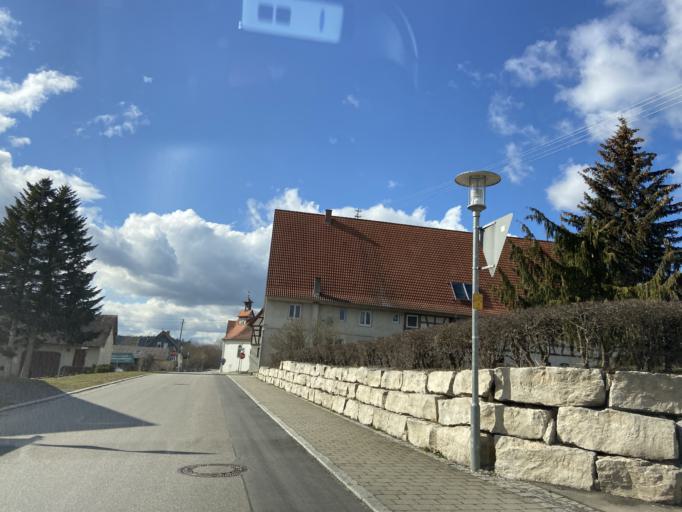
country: DE
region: Baden-Wuerttemberg
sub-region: Tuebingen Region
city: Ostrach
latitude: 47.9691
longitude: 9.3677
